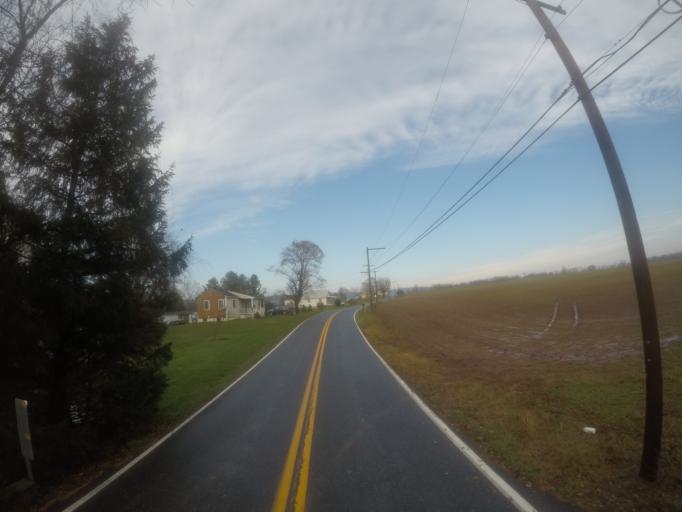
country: US
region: Maryland
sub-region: Frederick County
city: Walkersville
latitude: 39.5277
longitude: -77.4023
